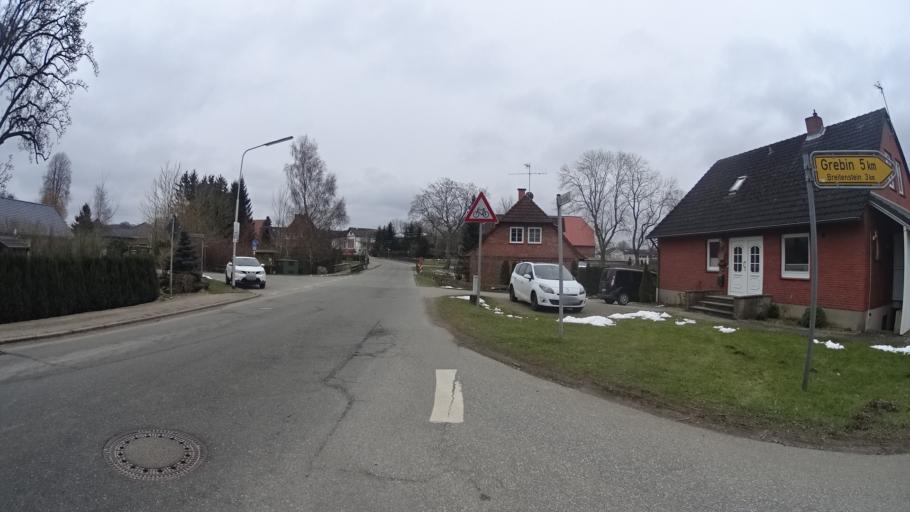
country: DE
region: Schleswig-Holstein
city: Neukirchen
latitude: 54.2050
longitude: 10.5574
